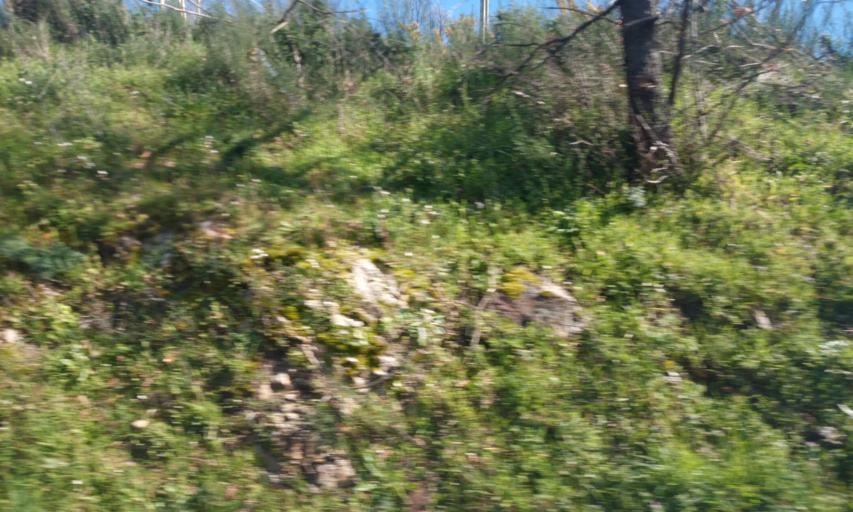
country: PT
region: Guarda
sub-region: Manteigas
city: Manteigas
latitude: 40.4877
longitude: -7.6060
